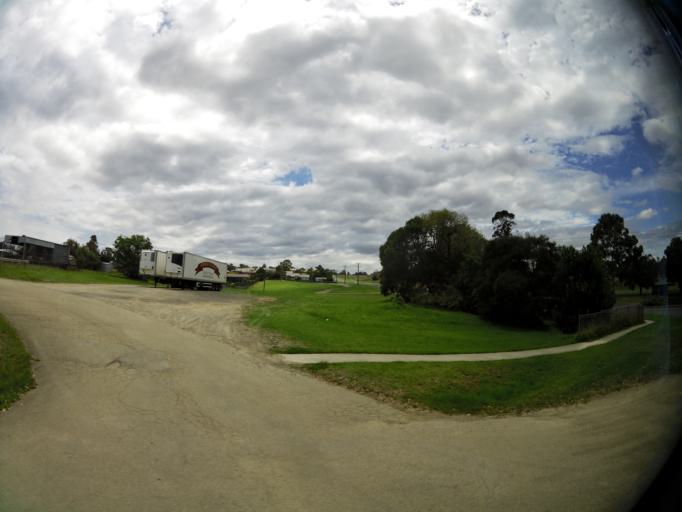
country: AU
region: Victoria
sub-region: East Gippsland
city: Lakes Entrance
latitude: -37.7058
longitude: 148.4651
